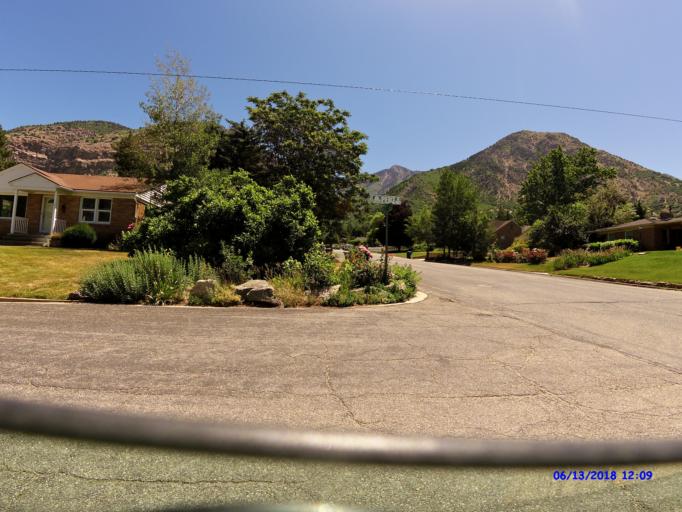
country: US
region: Utah
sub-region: Weber County
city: Ogden
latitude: 41.2161
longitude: -111.9348
